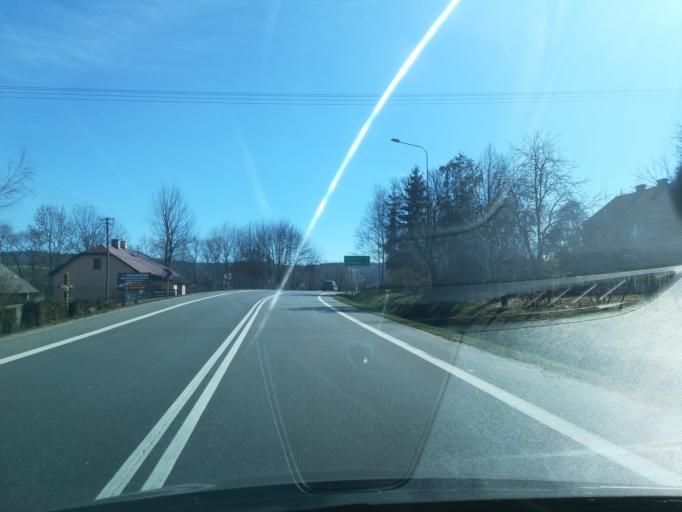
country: PL
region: Subcarpathian Voivodeship
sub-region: Powiat strzyzowski
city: Polomia
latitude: 49.8880
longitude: 21.8969
